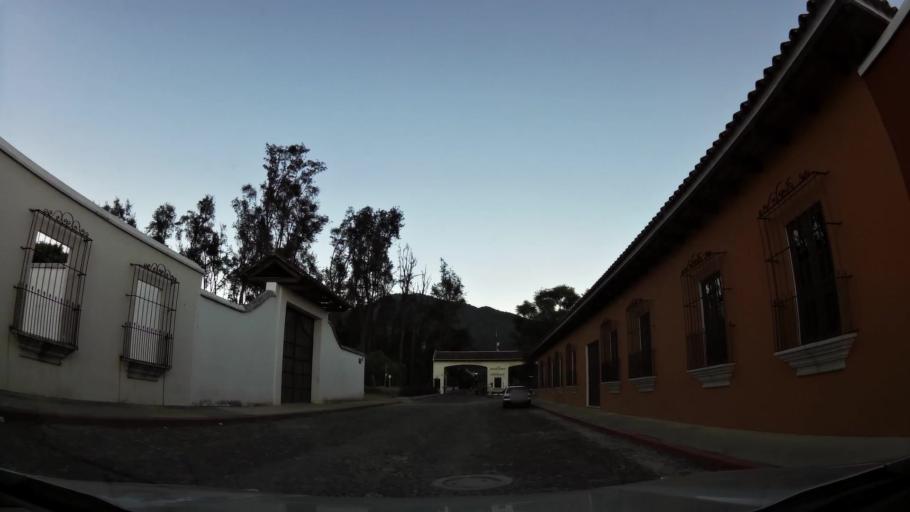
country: GT
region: Sacatepequez
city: Antigua Guatemala
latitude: 14.5606
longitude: -90.7258
